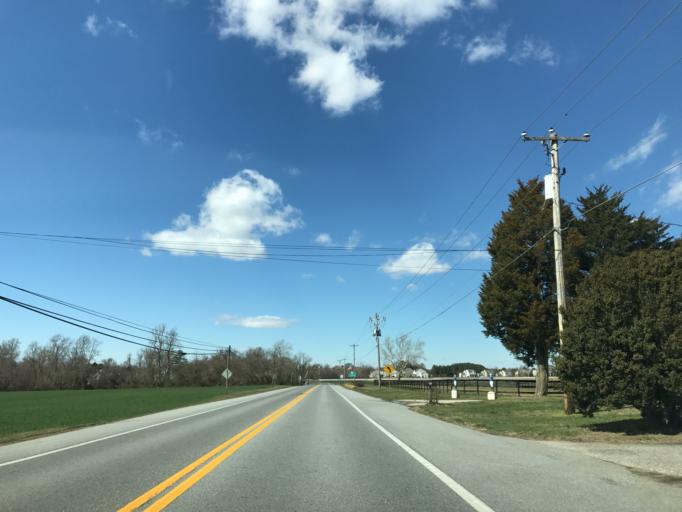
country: US
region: Maryland
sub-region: Queen Anne's County
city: Kingstown
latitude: 39.1365
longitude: -75.9780
